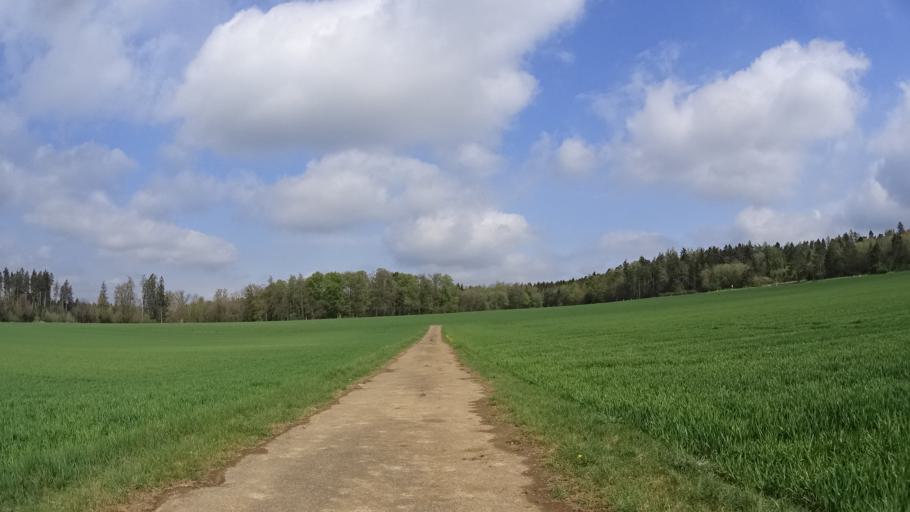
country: DE
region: Bavaria
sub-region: Upper Bavaria
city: Bohmfeld
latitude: 48.8894
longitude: 11.4023
